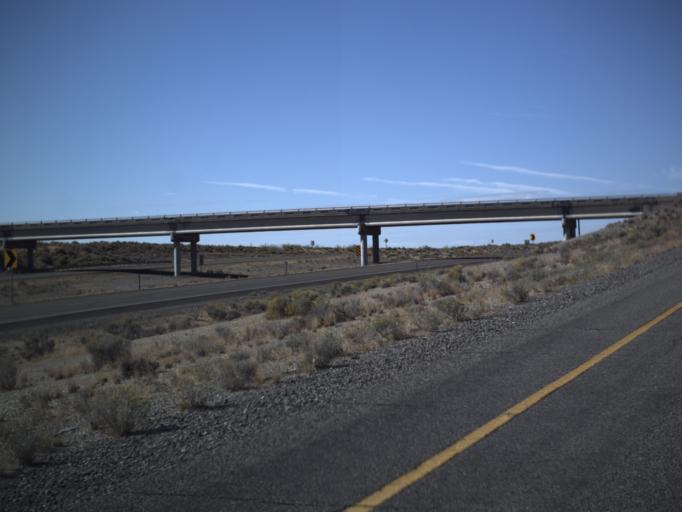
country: US
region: Utah
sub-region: Tooele County
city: Grantsville
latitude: 40.7701
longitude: -112.9831
